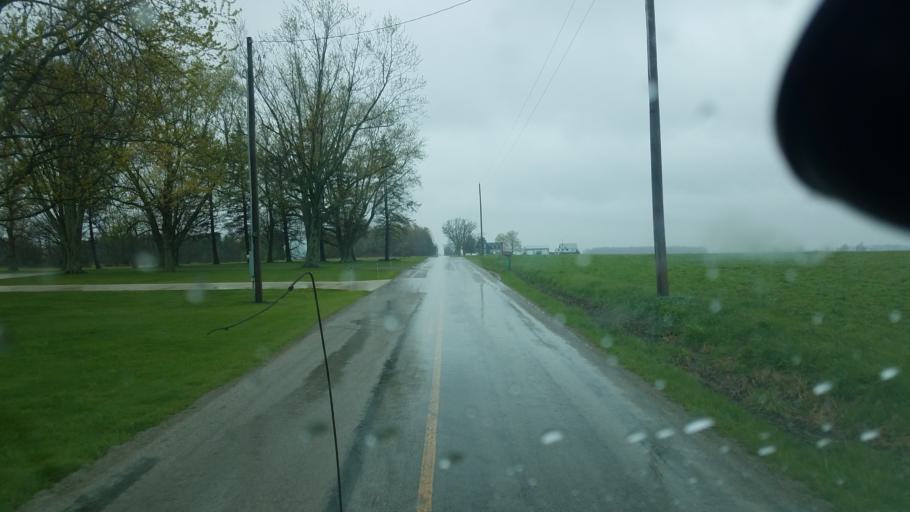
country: US
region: Ohio
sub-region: Union County
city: Richwood
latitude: 40.5224
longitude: -83.3934
